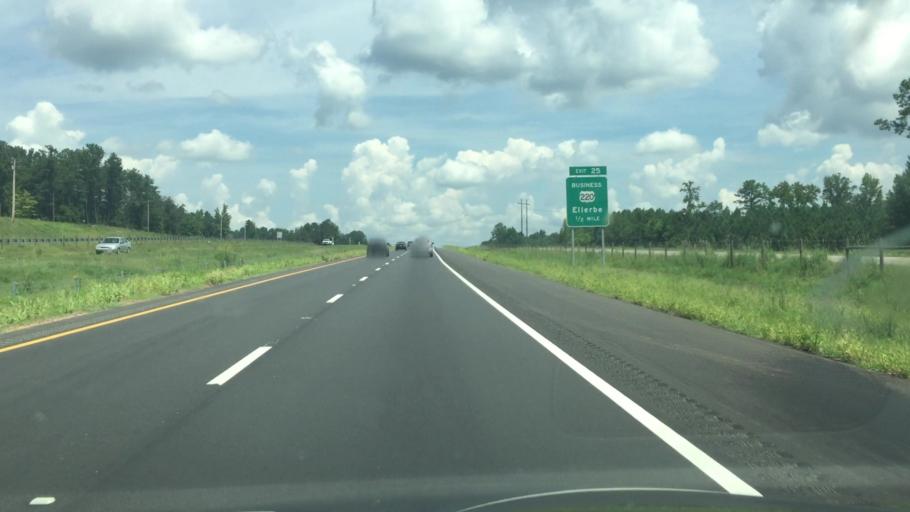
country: US
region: North Carolina
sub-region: Richmond County
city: Ellerbe
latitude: 35.0317
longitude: -79.7692
